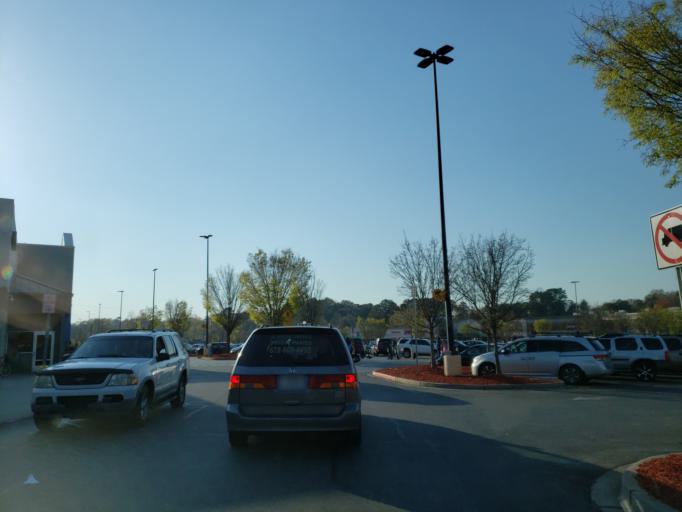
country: US
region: Georgia
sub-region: Cobb County
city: Marietta
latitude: 33.9464
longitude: -84.5205
